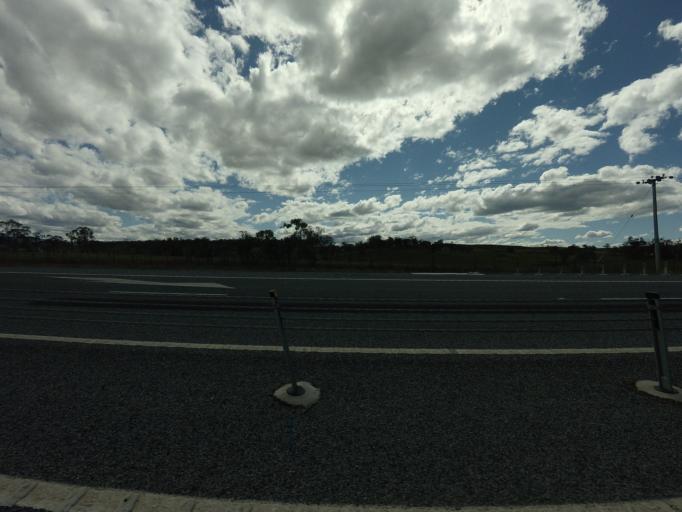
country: AU
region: Tasmania
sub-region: Northern Midlands
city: Evandale
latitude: -42.0815
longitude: 147.4563
